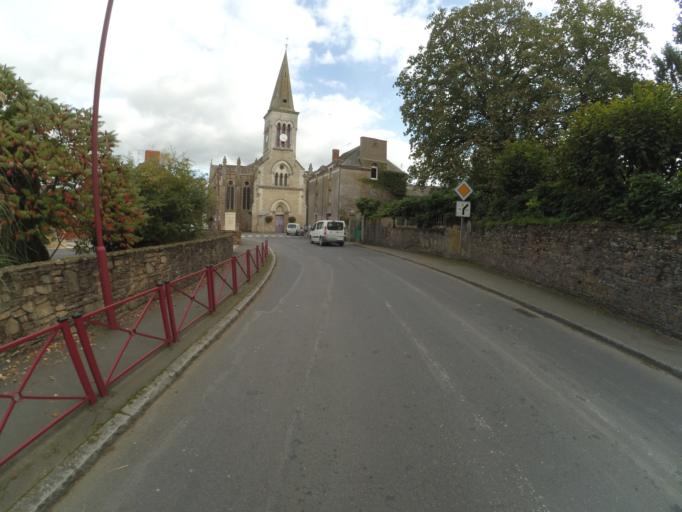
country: FR
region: Pays de la Loire
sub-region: Departement de la Loire-Atlantique
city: Fay-de-Bretagne
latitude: 47.4154
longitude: -1.7926
